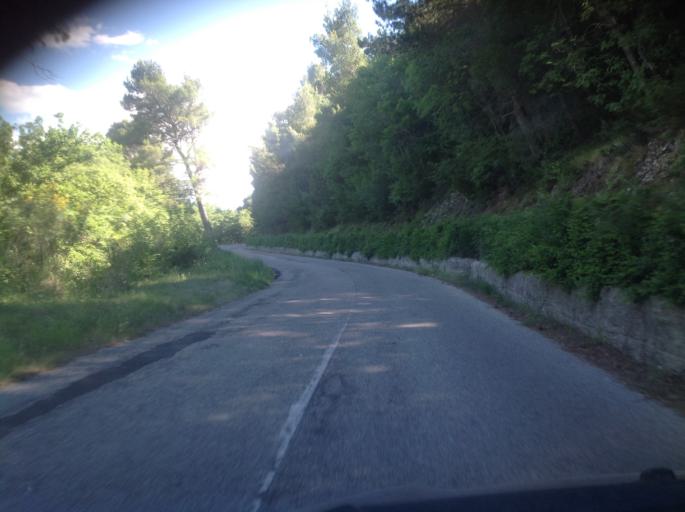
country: IT
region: Umbria
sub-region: Provincia di Terni
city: Stroncone
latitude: 42.4817
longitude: 12.6696
